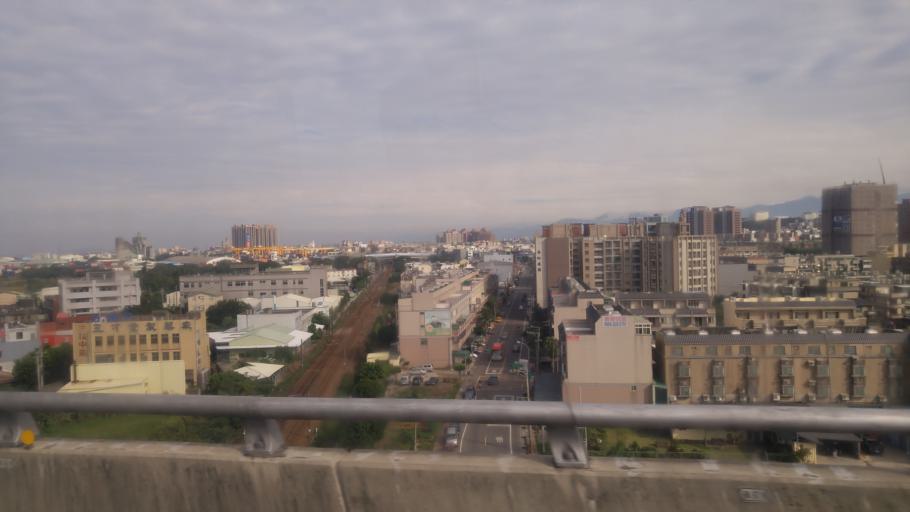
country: TW
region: Taiwan
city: Daxi
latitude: 24.9132
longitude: 121.1662
